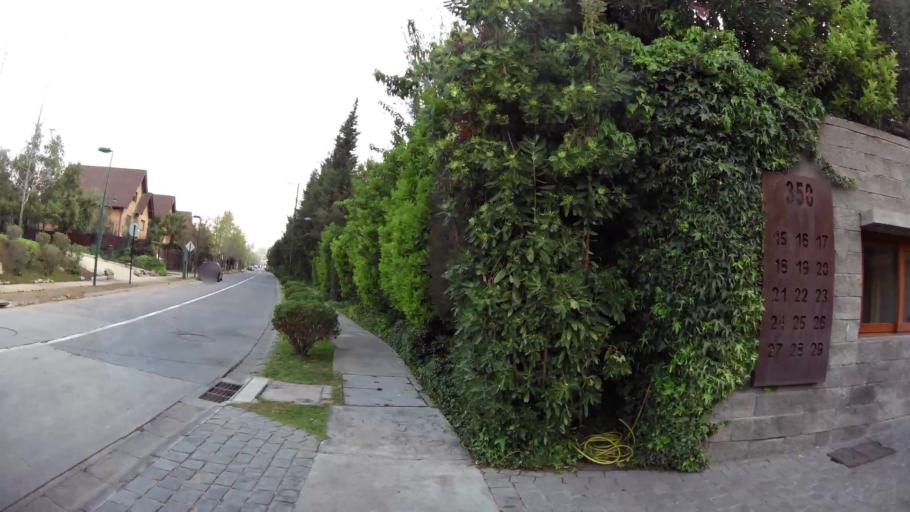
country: CL
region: Santiago Metropolitan
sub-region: Provincia de Santiago
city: Villa Presidente Frei, Nunoa, Santiago, Chile
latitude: -33.3554
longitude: -70.5467
